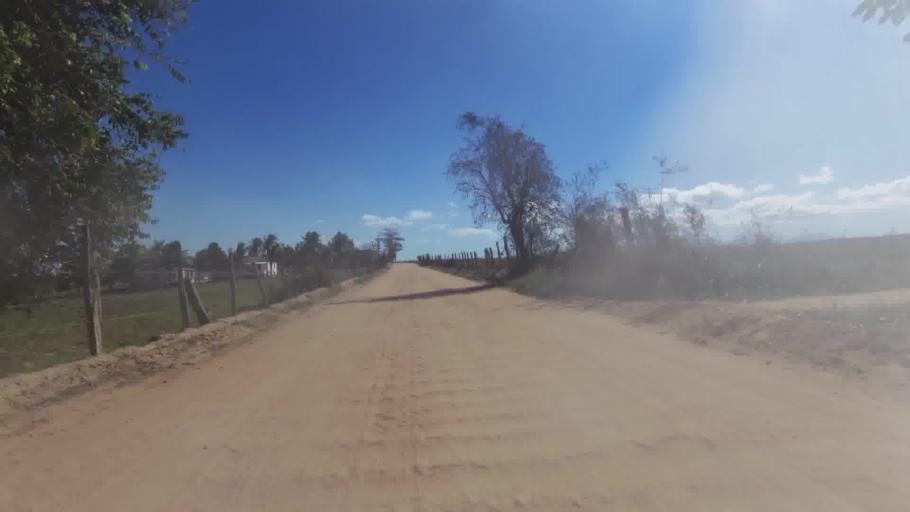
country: BR
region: Espirito Santo
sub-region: Marataizes
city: Marataizes
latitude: -21.1573
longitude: -40.9756
